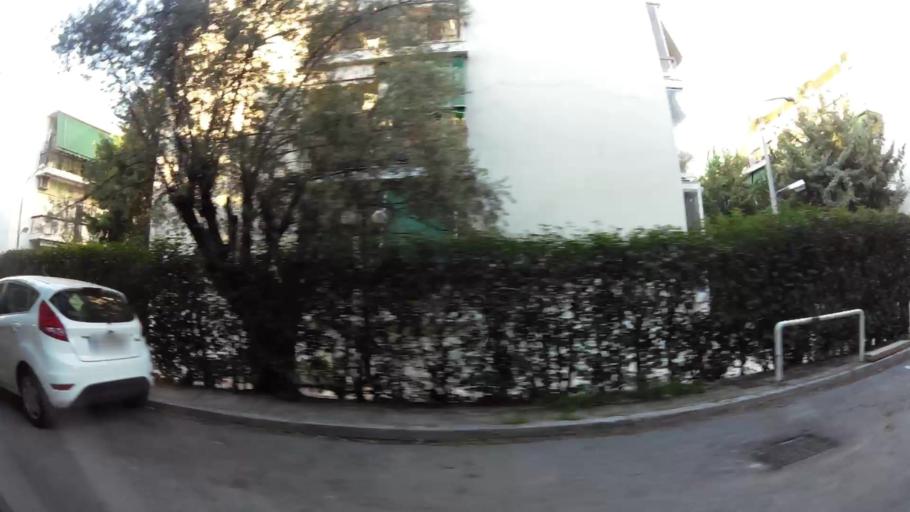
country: GR
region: Attica
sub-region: Nomarchia Athinas
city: Kifisia
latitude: 38.0709
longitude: 23.8023
